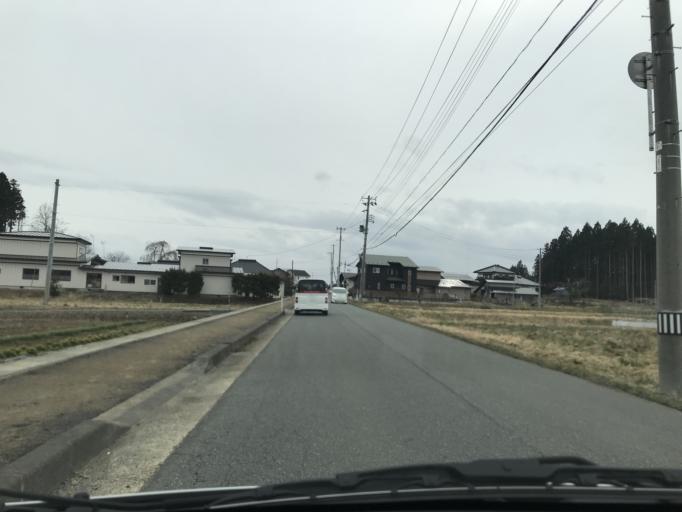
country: JP
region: Iwate
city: Hanamaki
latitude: 39.3450
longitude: 141.0979
